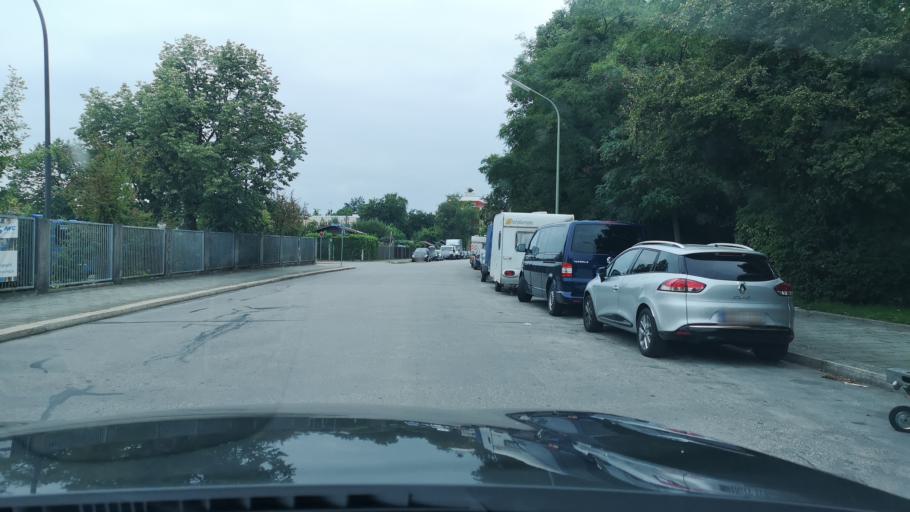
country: DE
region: Bavaria
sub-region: Upper Bavaria
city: Munich
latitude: 48.1334
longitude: 11.5168
